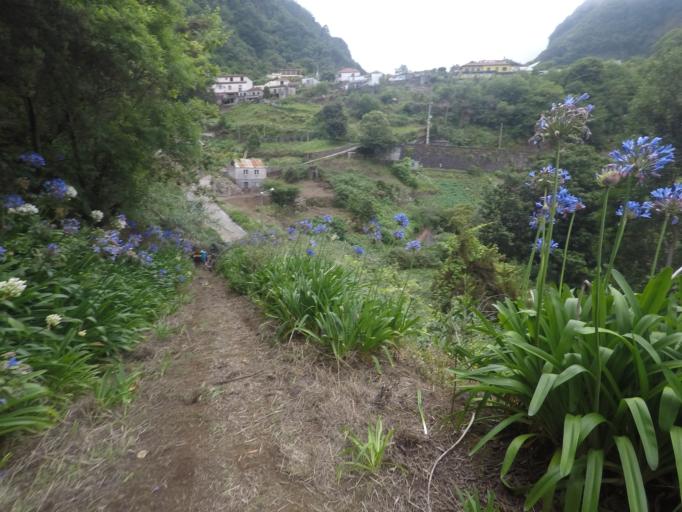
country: PT
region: Madeira
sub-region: Santana
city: Santana
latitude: 32.7545
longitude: -16.8766
